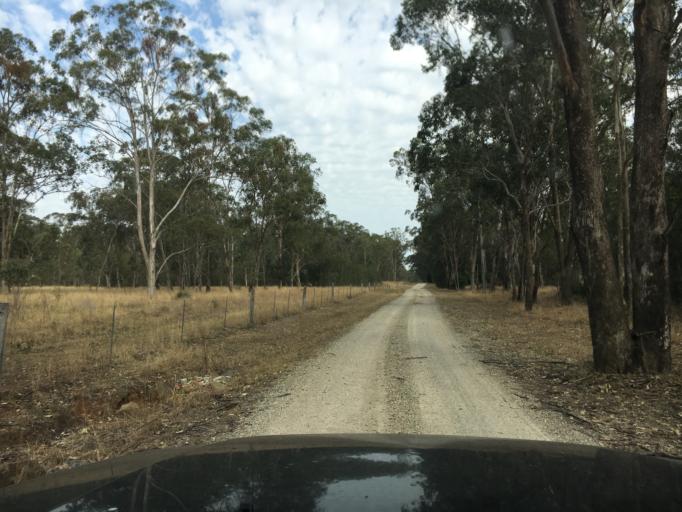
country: AU
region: New South Wales
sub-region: Cessnock
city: Branxton
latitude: -32.6657
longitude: 151.3028
